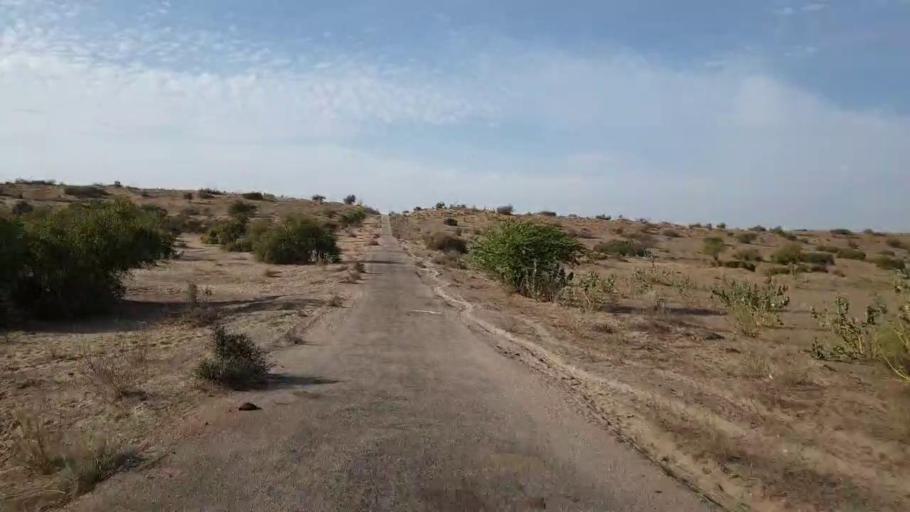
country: PK
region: Sindh
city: Nabisar
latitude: 25.0045
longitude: 69.9229
